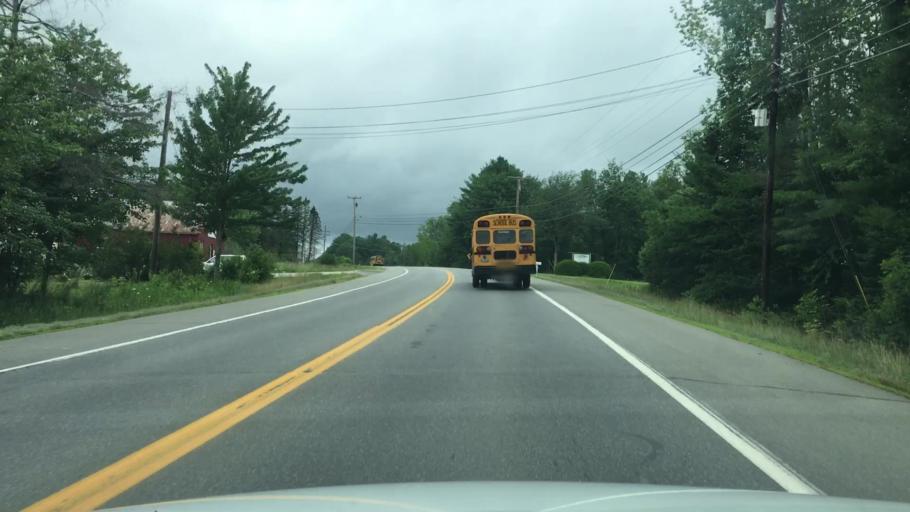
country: US
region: Maine
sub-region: Kennebec County
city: Windsor
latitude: 44.2687
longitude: -69.5684
